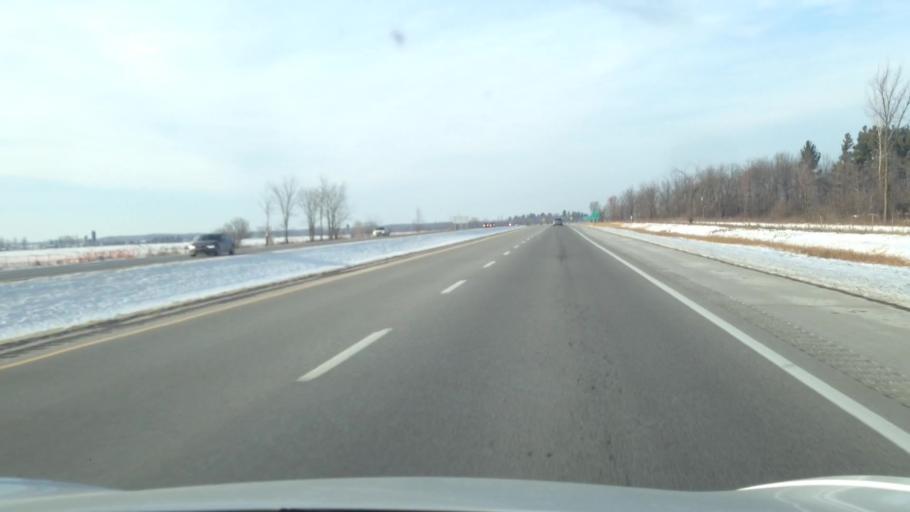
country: CA
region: Quebec
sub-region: Monteregie
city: Rigaud
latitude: 45.5064
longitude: -74.3663
